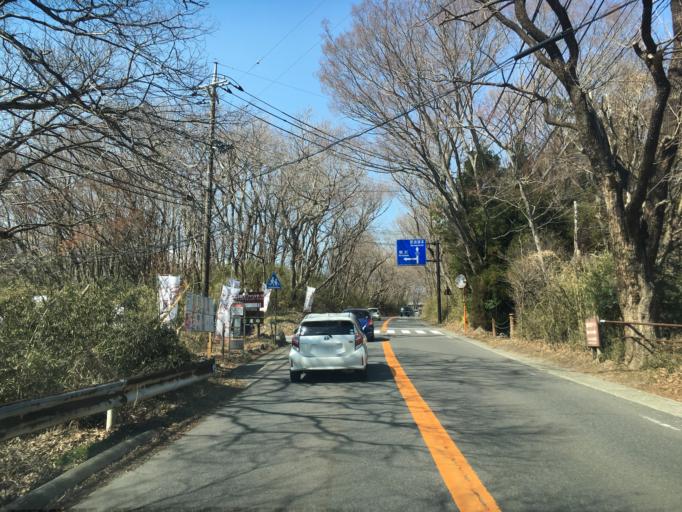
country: JP
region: Tochigi
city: Kuroiso
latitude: 37.0577
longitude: 140.0126
